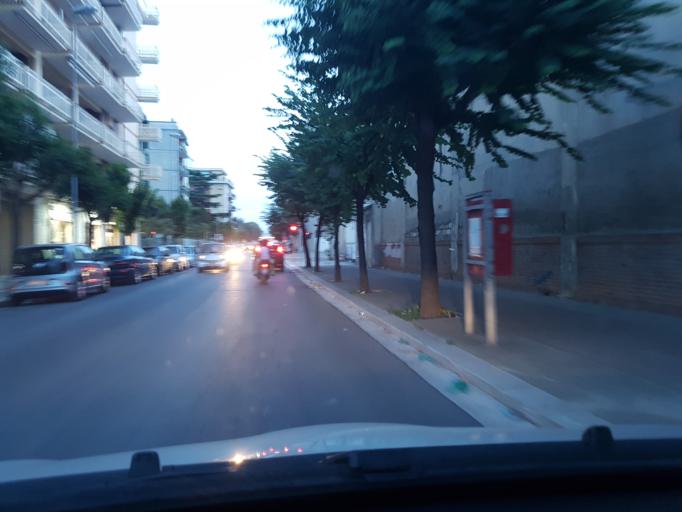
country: IT
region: Apulia
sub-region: Provincia di Foggia
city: Cerignola
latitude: 41.2623
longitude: 15.9079
